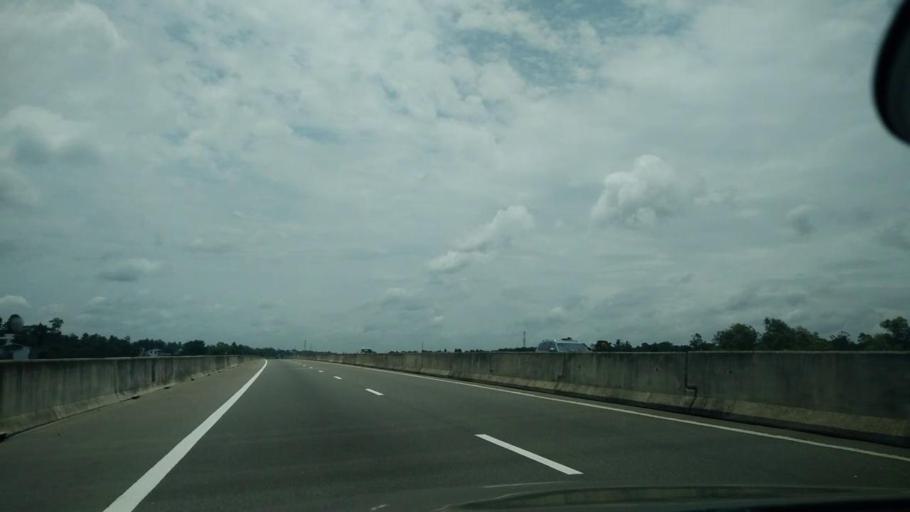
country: LK
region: Western
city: Mulleriyawa
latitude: 6.8994
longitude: 79.9793
